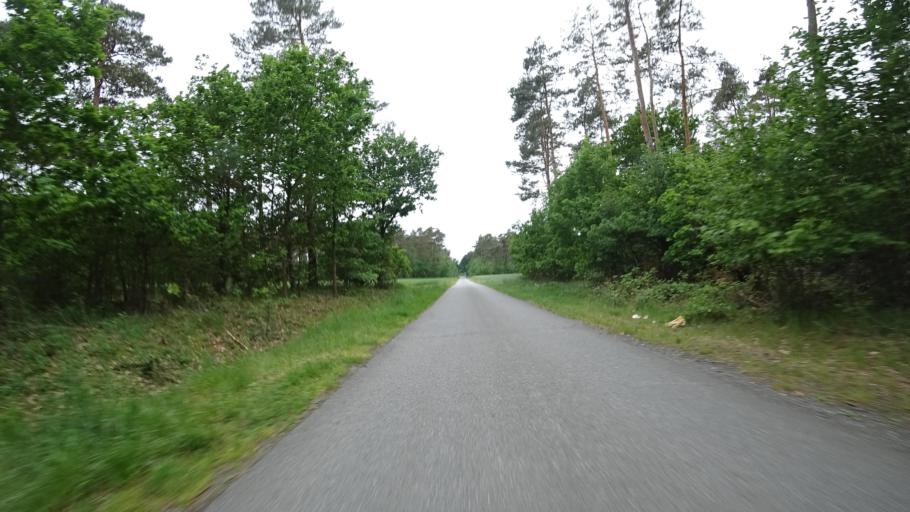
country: DE
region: North Rhine-Westphalia
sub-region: Regierungsbezirk Detmold
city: Rheda-Wiedenbruck
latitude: 51.9076
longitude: 8.2879
